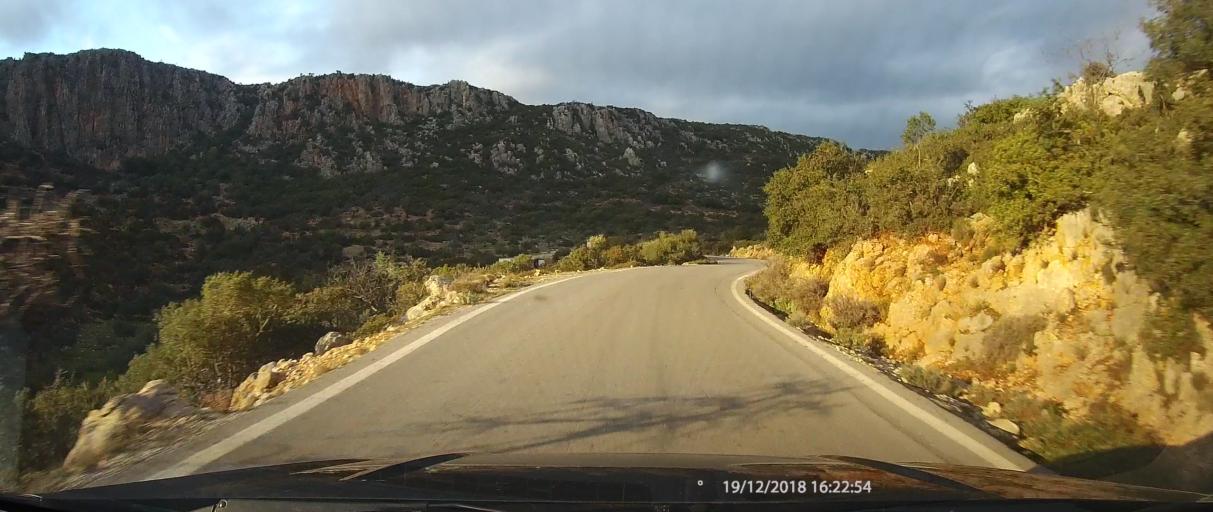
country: GR
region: Peloponnese
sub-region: Nomos Lakonias
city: Kato Glikovrisi
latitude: 36.9459
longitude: 22.8319
